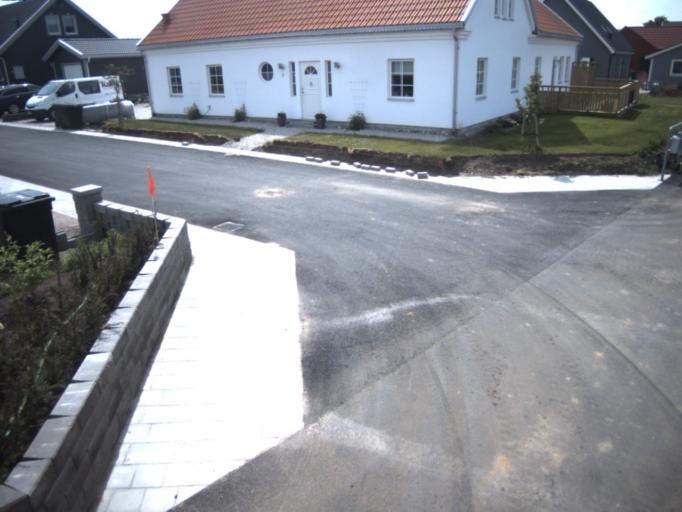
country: SE
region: Skane
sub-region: Helsingborg
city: Helsingborg
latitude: 56.1003
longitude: 12.6605
